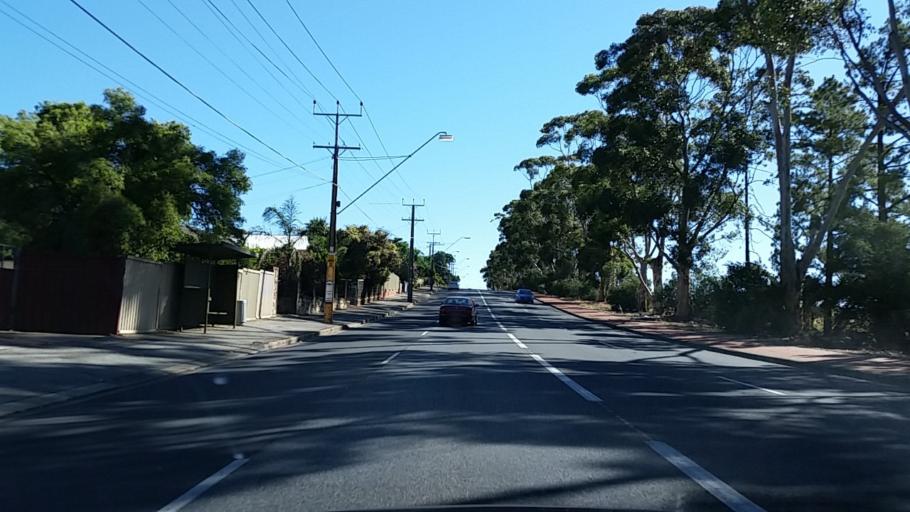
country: AU
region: South Australia
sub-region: Salisbury
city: Ingle Farm
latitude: -34.8391
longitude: 138.6233
